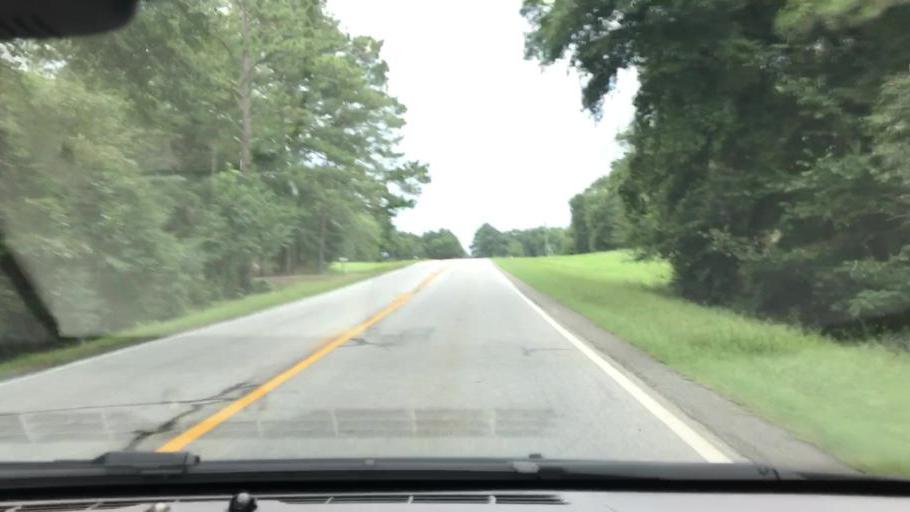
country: US
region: Georgia
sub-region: Early County
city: Blakely
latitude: 31.2802
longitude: -85.0811
